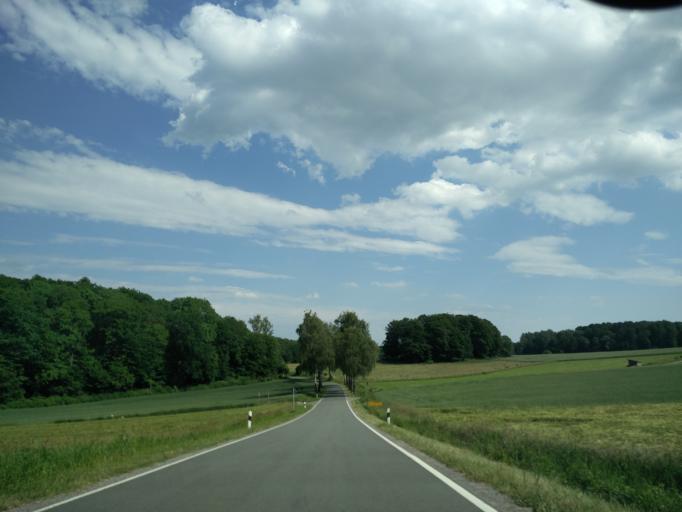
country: DE
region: North Rhine-Westphalia
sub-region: Regierungsbezirk Detmold
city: Willebadessen
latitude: 51.6592
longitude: 9.0277
